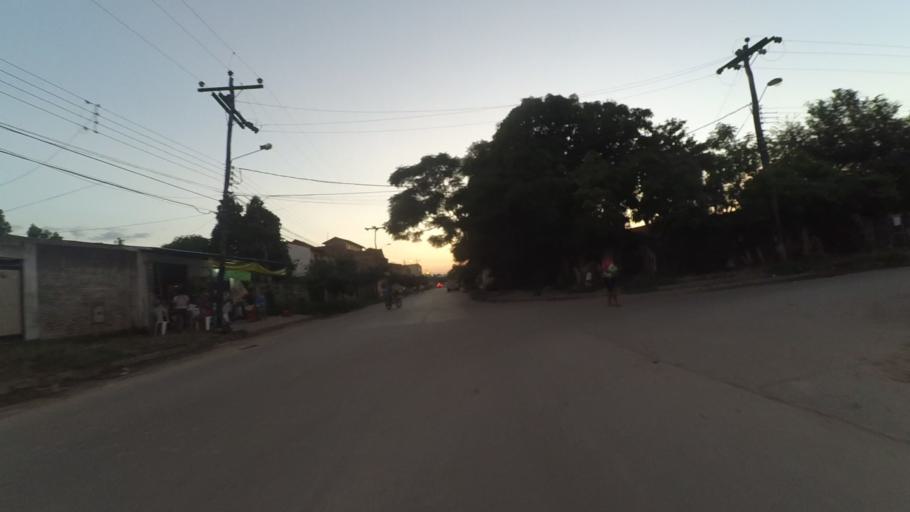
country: BO
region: Santa Cruz
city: Santa Cruz de la Sierra
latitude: -17.8211
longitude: -63.1335
